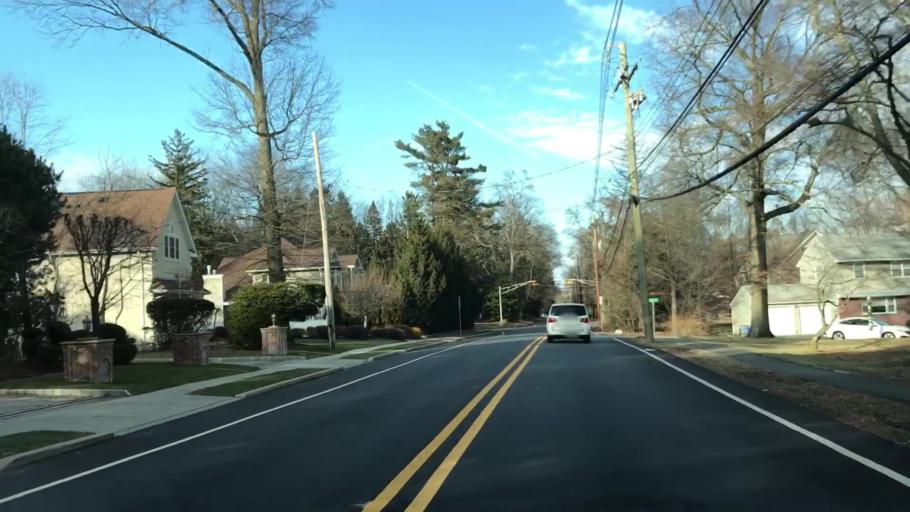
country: US
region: New Jersey
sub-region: Bergen County
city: Harrington Park
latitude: 40.9765
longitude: -73.9730
